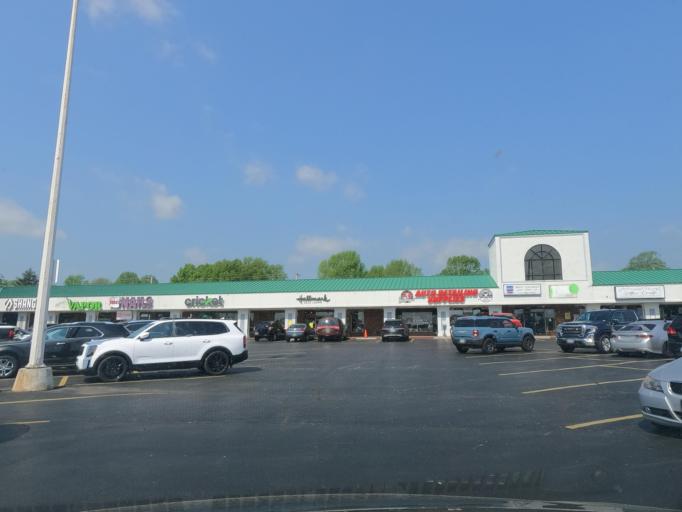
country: US
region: Missouri
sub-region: Greene County
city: Springfield
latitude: 37.1435
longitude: -93.2967
